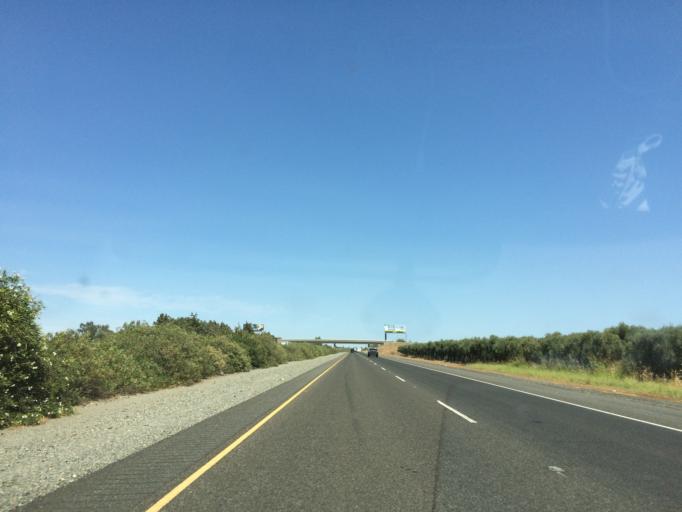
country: US
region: California
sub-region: Glenn County
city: Orland
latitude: 39.6935
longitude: -122.2050
